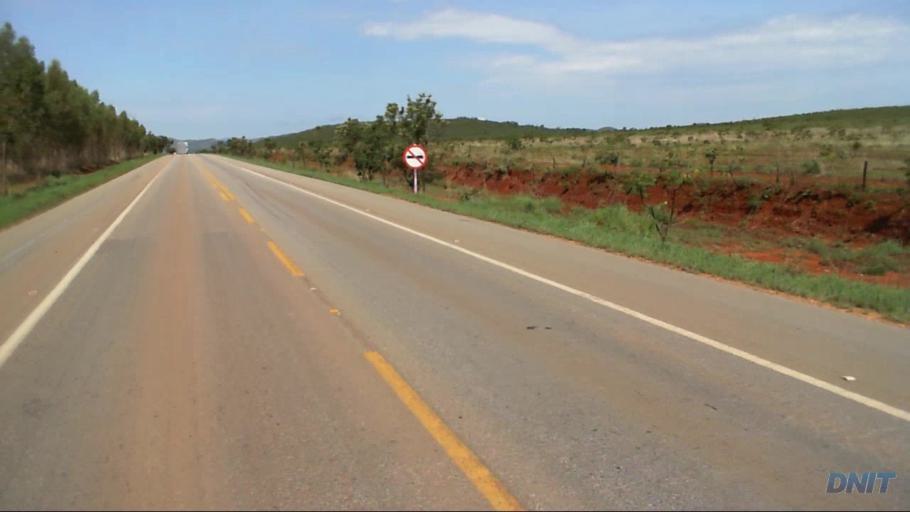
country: BR
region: Goias
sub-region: Barro Alto
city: Barro Alto
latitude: -15.2039
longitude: -48.7398
